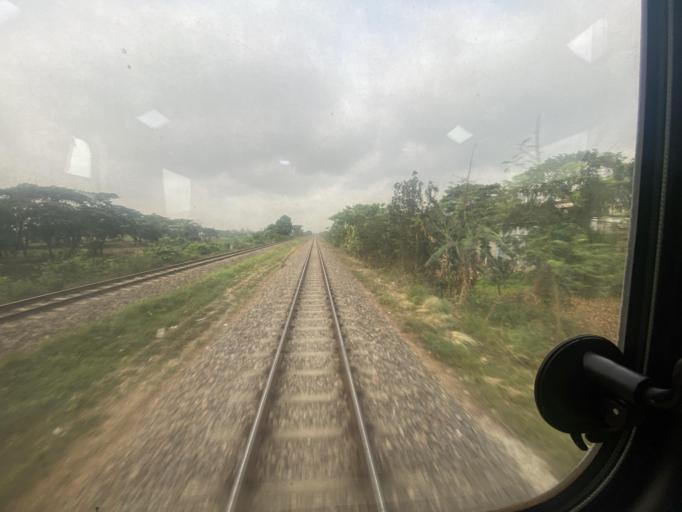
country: BD
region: Dhaka
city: Tungi
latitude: 23.9170
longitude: 90.4299
